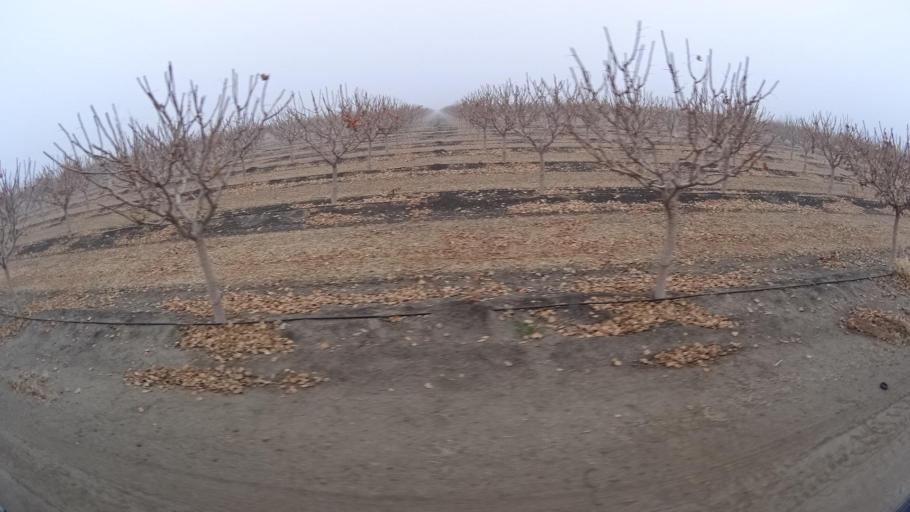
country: US
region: California
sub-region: Kern County
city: Buttonwillow
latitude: 35.4595
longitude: -119.5649
